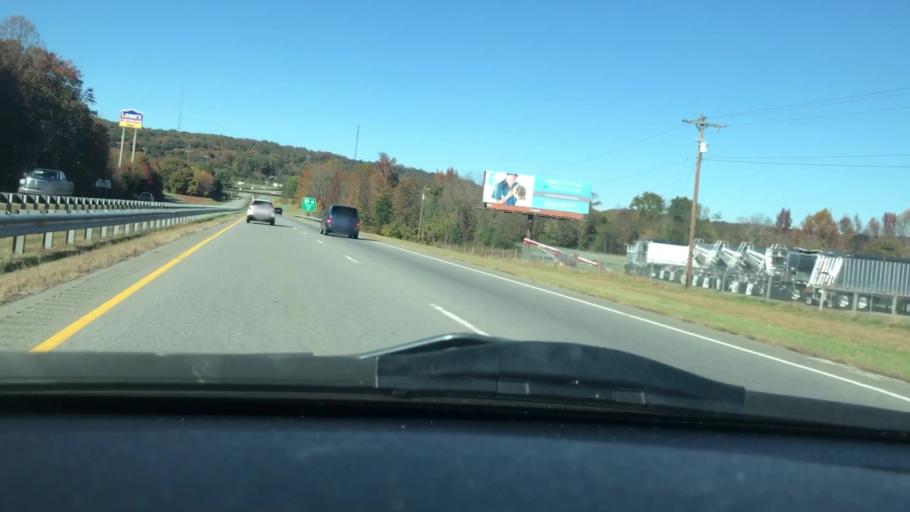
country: US
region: North Carolina
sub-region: Rockingham County
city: Mayodan
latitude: 36.4100
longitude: -79.9377
